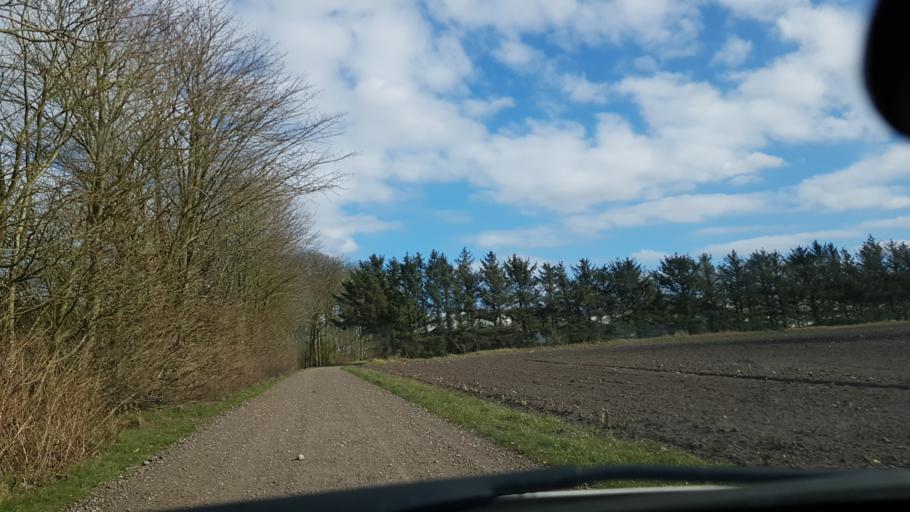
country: DK
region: South Denmark
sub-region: Esbjerg Kommune
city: Ribe
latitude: 55.2881
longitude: 8.8391
